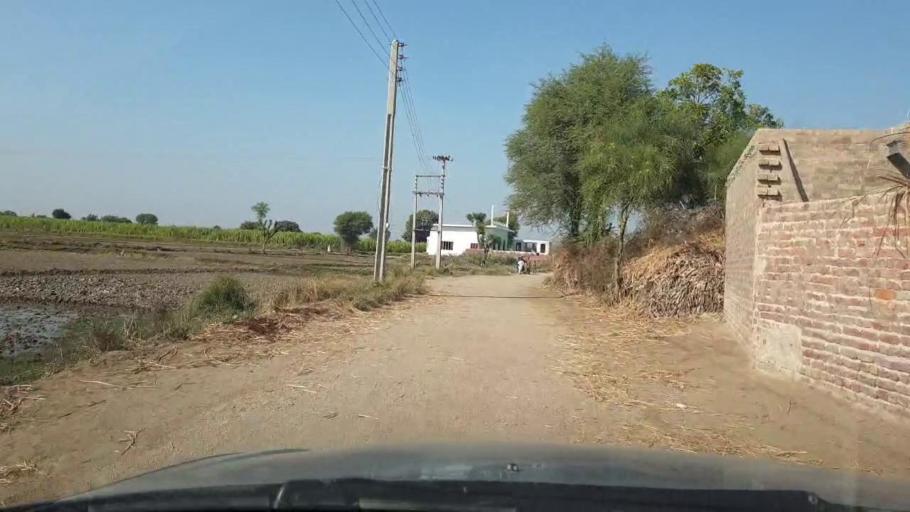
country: PK
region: Sindh
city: Tando Muhammad Khan
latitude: 25.1158
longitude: 68.5899
